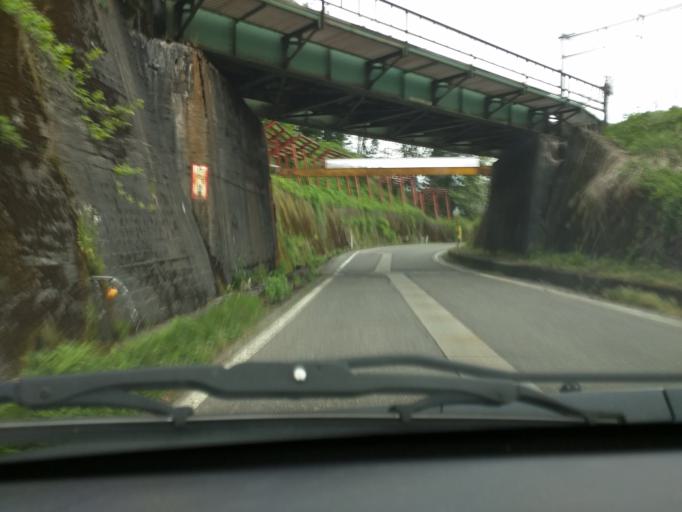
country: JP
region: Niigata
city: Muikamachi
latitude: 37.2082
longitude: 138.9511
